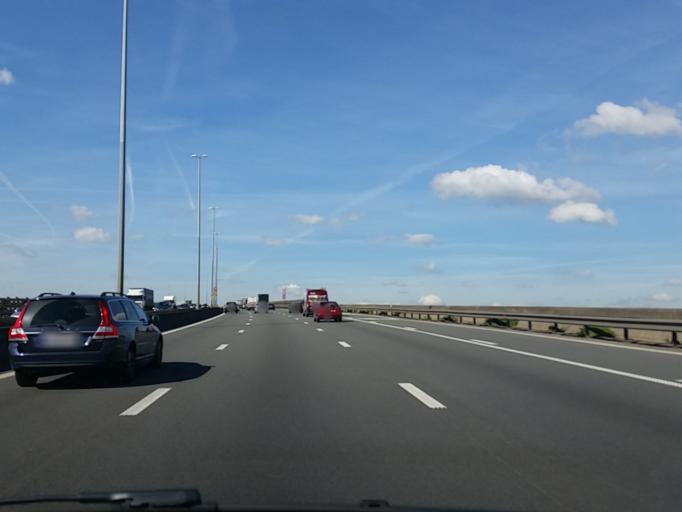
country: BE
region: Flanders
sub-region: Provincie Vlaams-Brabant
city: Machelen
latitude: 50.9114
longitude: 4.4262
